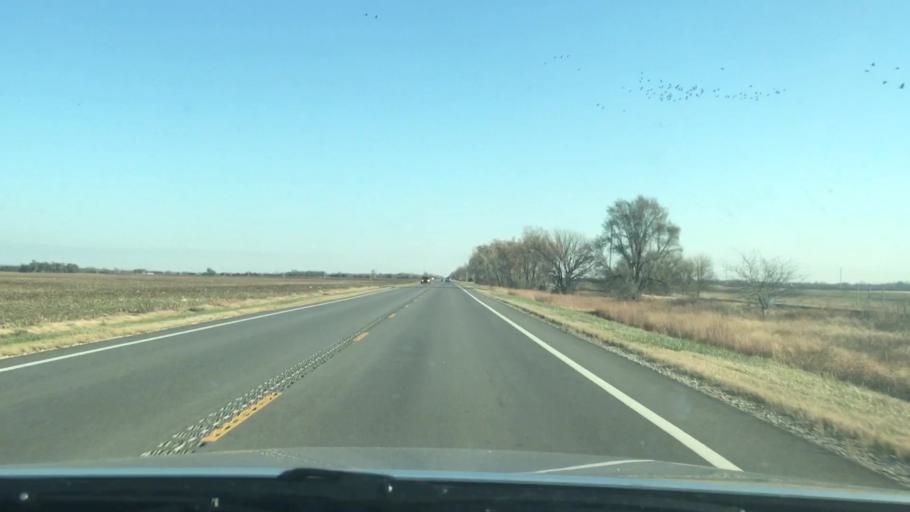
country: US
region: Kansas
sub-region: Reno County
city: Nickerson
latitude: 38.1342
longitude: -98.0645
